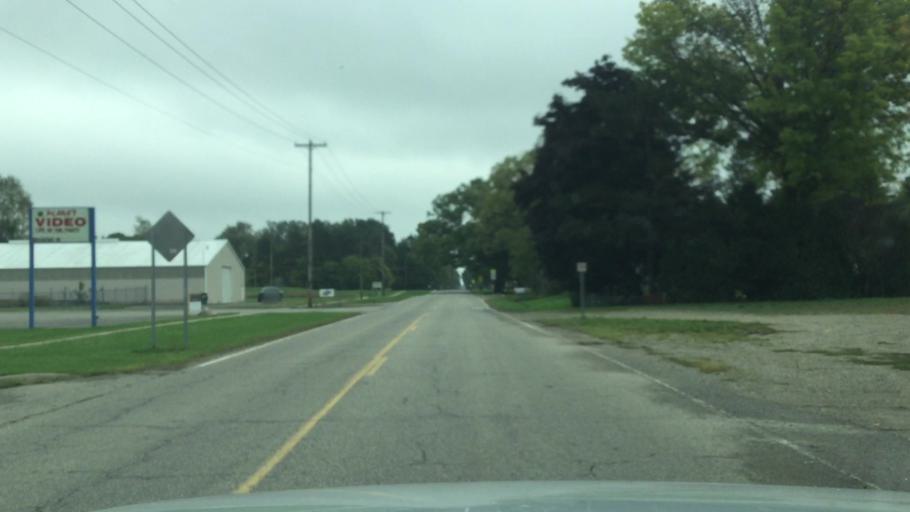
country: US
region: Michigan
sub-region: Shiawassee County
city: Perry
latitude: 42.8341
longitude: -84.2178
